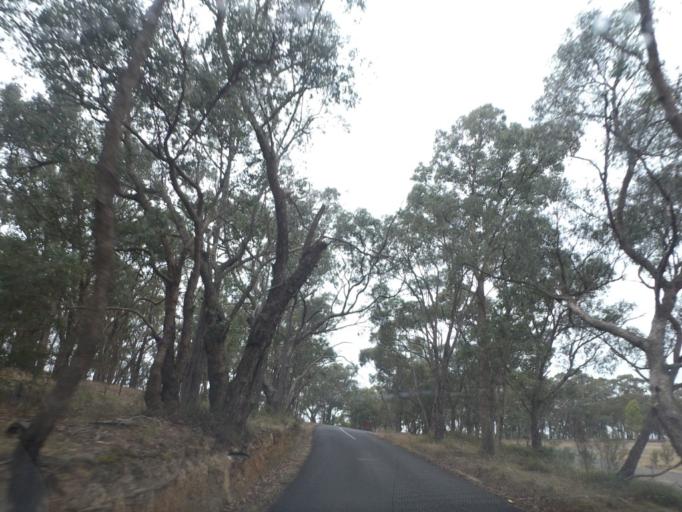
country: AU
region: Victoria
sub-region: Nillumbik
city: Saint Andrews
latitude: -37.6288
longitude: 145.2793
